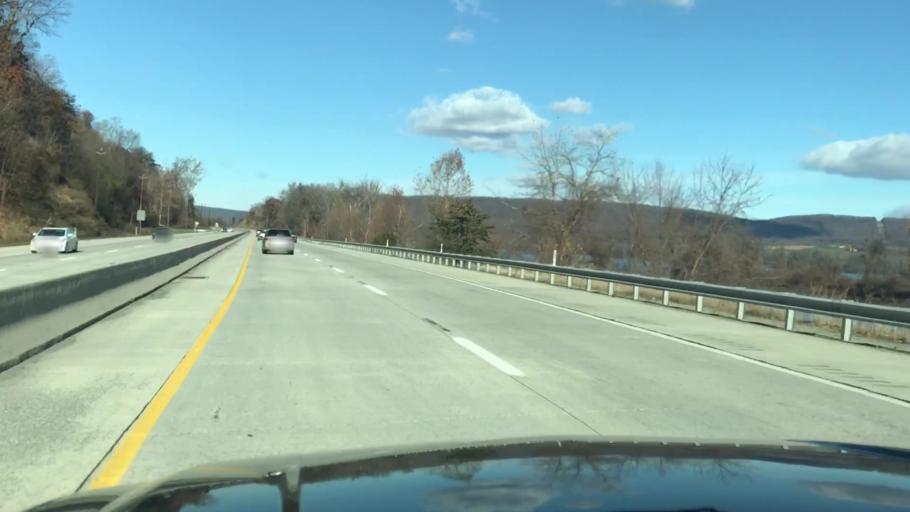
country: US
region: Pennsylvania
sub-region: Dauphin County
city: Matamoras
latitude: 40.4855
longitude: -76.9504
